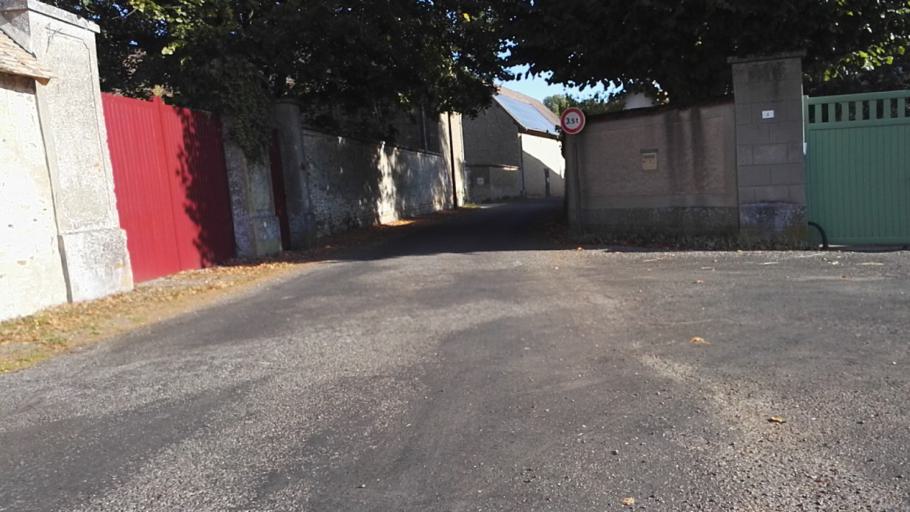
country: FR
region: Haute-Normandie
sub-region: Departement de l'Eure
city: Menilles
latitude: 49.0420
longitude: 1.3402
